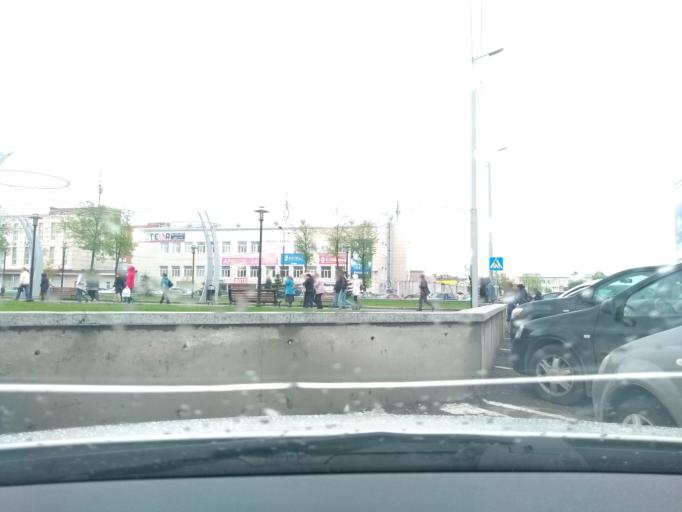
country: RU
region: Perm
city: Perm
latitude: 57.9830
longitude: 56.2530
